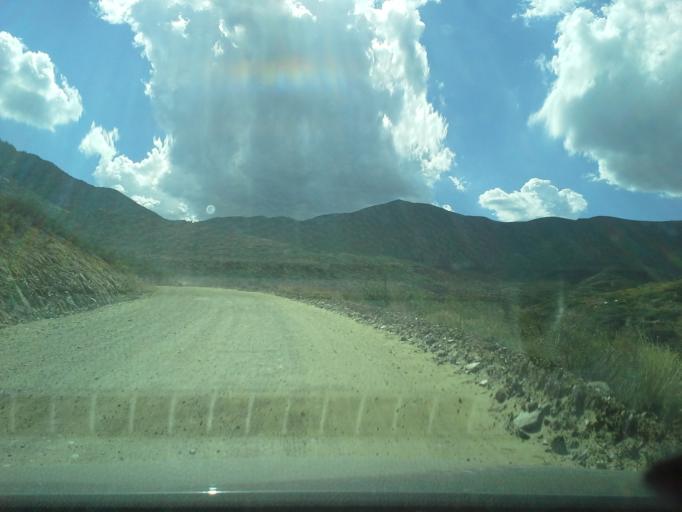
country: US
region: Arizona
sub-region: Yavapai County
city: Mayer
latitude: 34.2576
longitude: -112.2938
